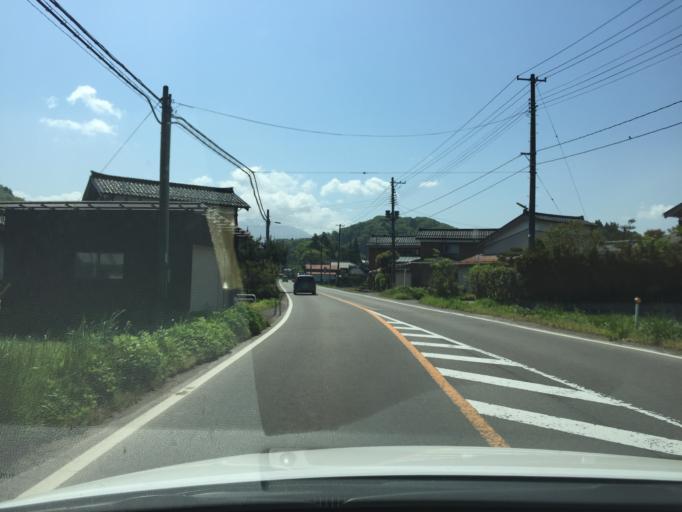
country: JP
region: Niigata
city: Kamo
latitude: 37.6308
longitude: 139.0947
